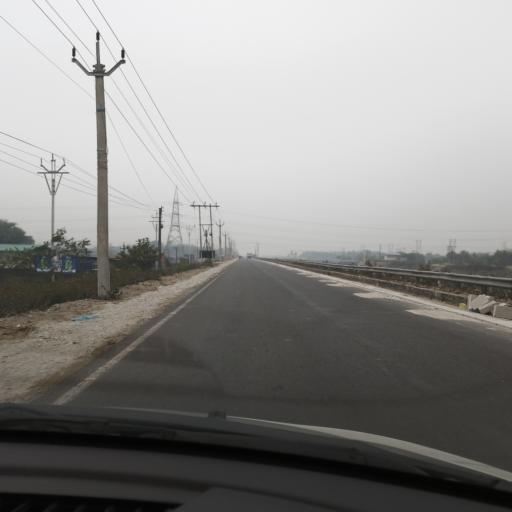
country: IN
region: West Bengal
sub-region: Darjiling
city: Shiliguri
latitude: 26.6608
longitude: 88.4624
